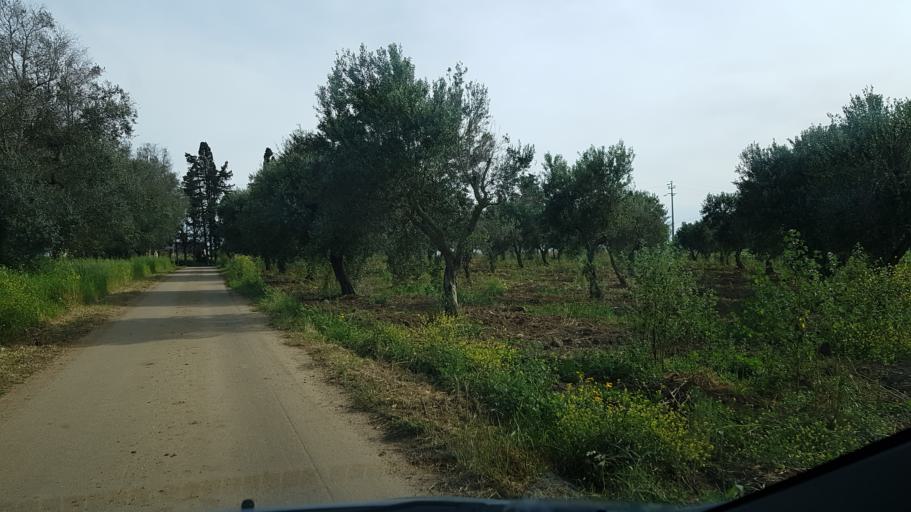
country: IT
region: Apulia
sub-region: Provincia di Brindisi
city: Tuturano
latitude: 40.5621
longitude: 17.9179
